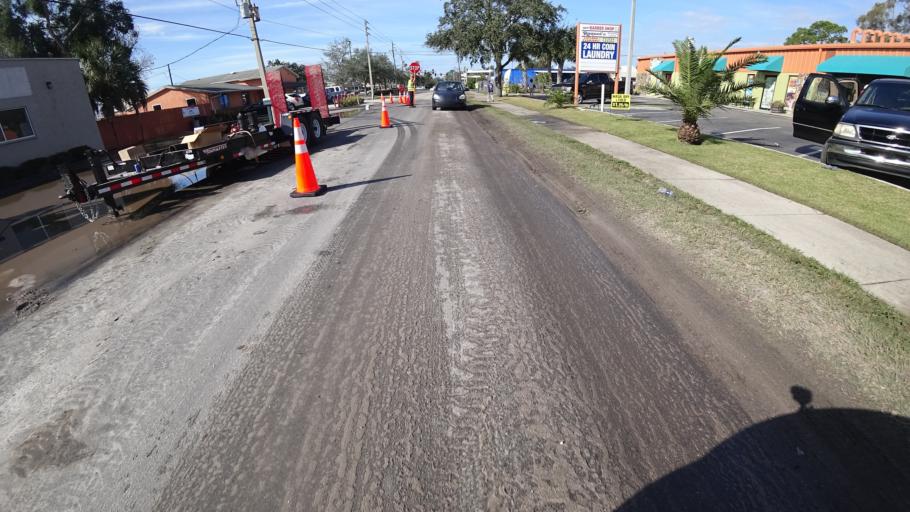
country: US
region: Florida
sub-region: Manatee County
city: Bayshore Gardens
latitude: 27.4349
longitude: -82.5740
